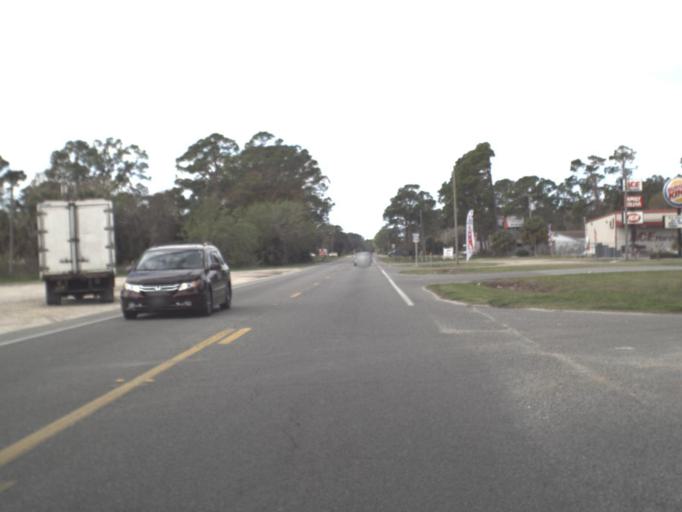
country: US
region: Florida
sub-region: Franklin County
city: Apalachicola
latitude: 29.7140
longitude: -85.0046
